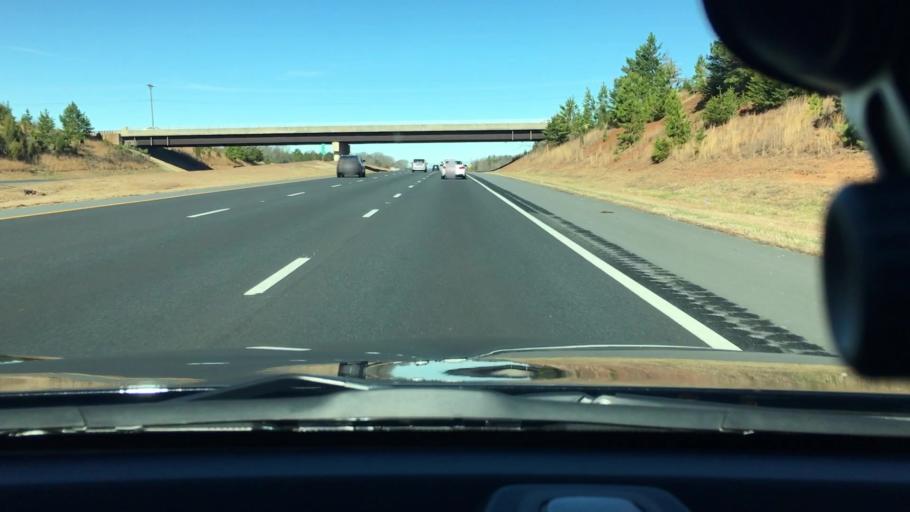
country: US
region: North Carolina
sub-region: Cabarrus County
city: Harrisburg
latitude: 35.2830
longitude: -80.6747
